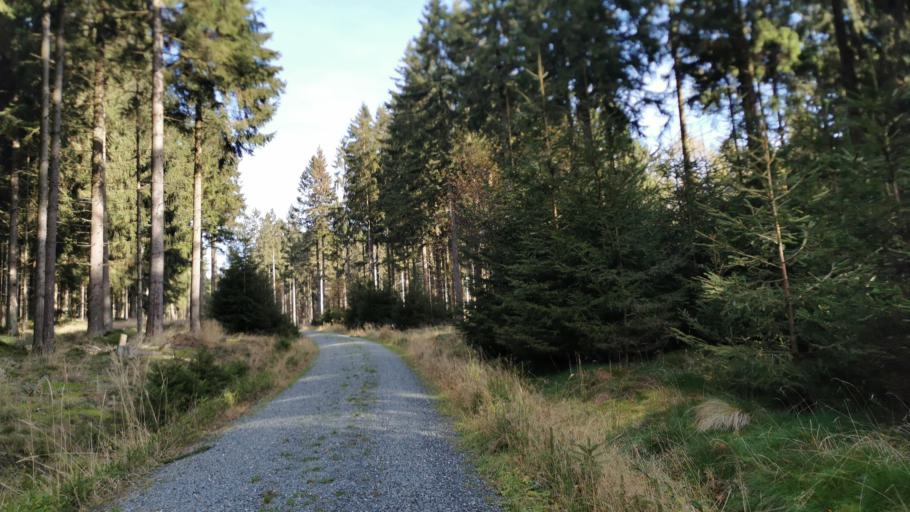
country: DE
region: Bavaria
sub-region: Upper Franconia
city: Tschirn
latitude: 50.4277
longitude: 11.4650
